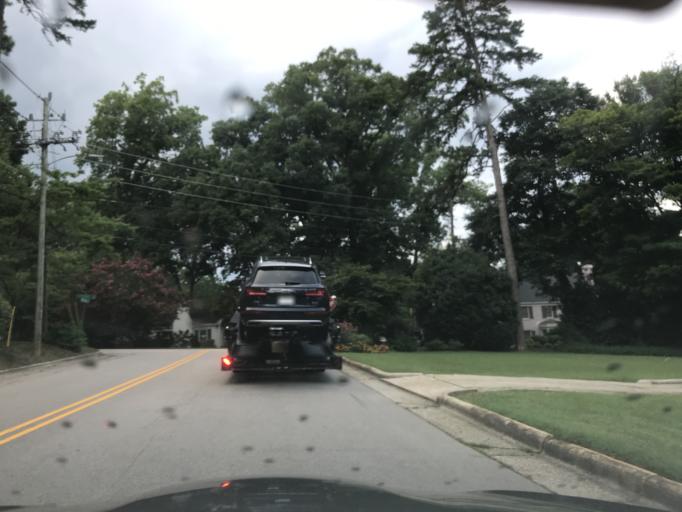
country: US
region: North Carolina
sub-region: Wake County
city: West Raleigh
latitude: 35.8118
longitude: -78.6659
